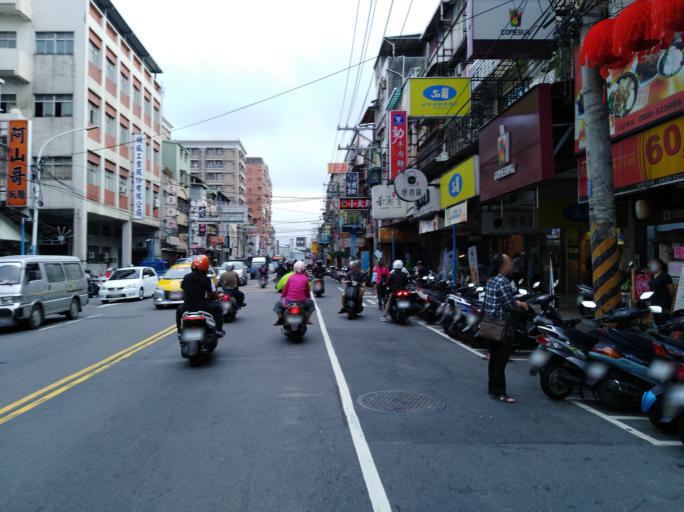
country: TW
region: Taipei
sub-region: Taipei
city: Banqiao
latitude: 25.0317
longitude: 121.4338
